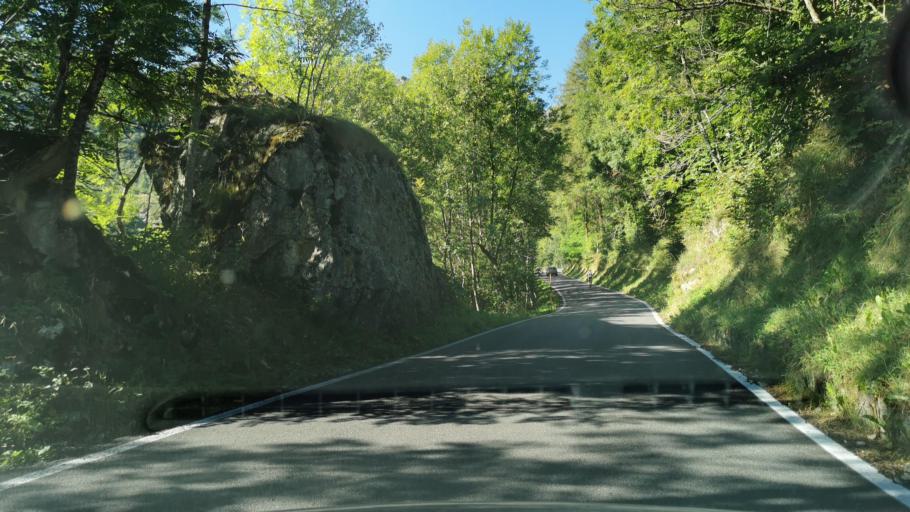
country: IT
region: Piedmont
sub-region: Provincia di Cuneo
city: Campomolino
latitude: 44.3980
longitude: 7.1982
